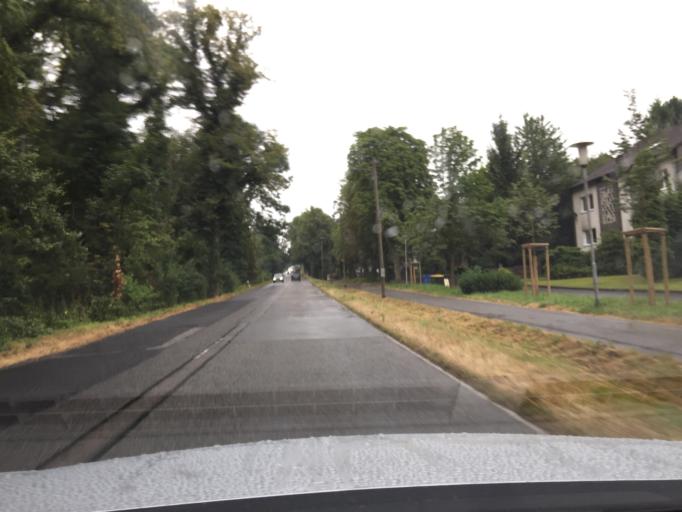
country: DE
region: North Rhine-Westphalia
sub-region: Regierungsbezirk Dusseldorf
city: Ratingen
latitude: 51.3391
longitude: 6.8971
